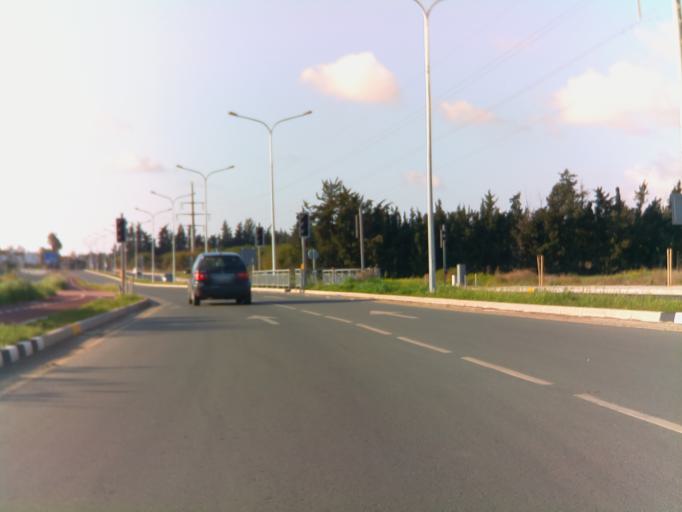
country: CY
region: Pafos
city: Paphos
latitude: 34.7487
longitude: 32.4341
